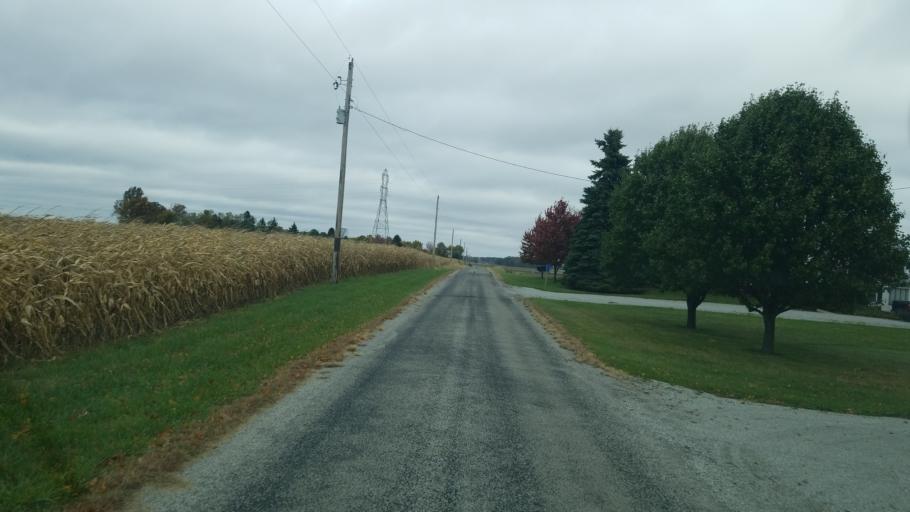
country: US
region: Ohio
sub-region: Crawford County
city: Bucyrus
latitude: 40.9228
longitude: -82.8452
